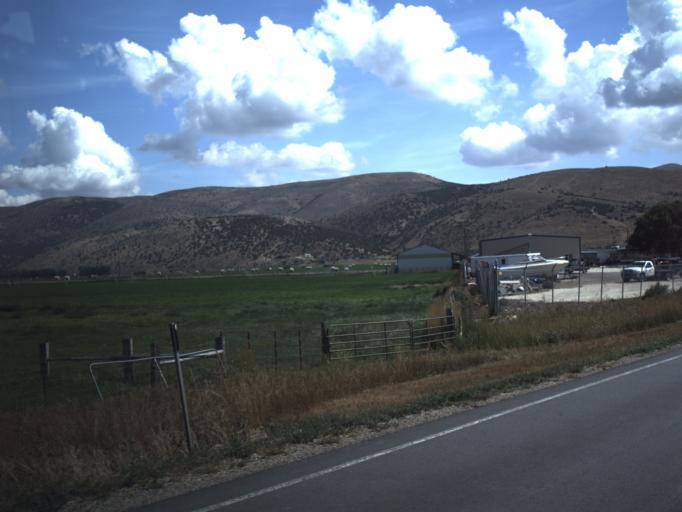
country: US
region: Utah
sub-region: Rich County
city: Randolph
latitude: 41.8330
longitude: -111.3258
